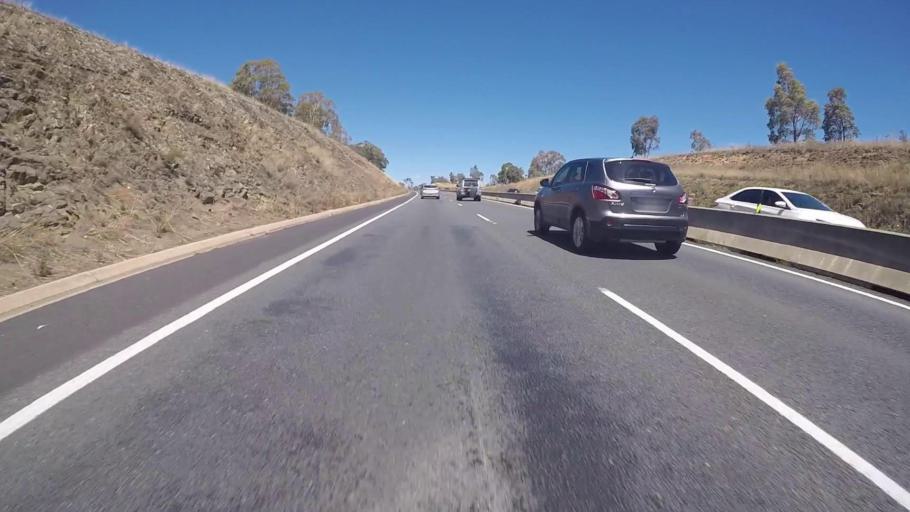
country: AU
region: Australian Capital Territory
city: Forrest
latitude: -35.3291
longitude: 149.0636
